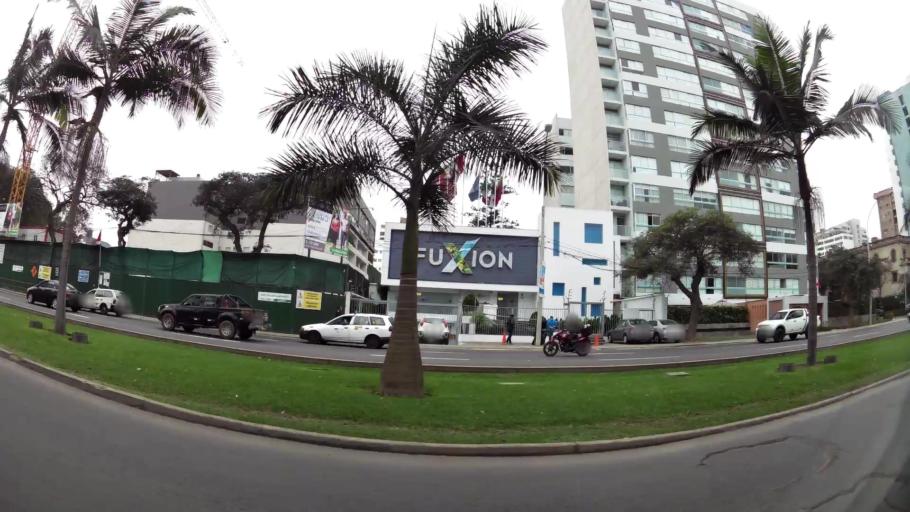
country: PE
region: Lima
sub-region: Lima
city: San Isidro
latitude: -12.0947
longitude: -77.0501
